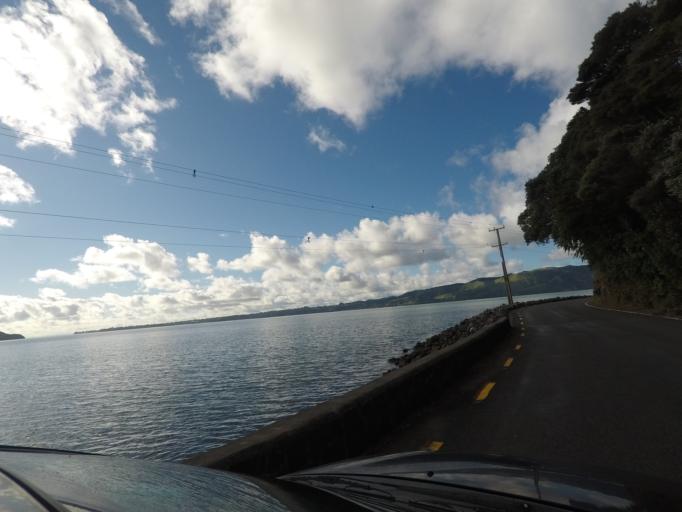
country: NZ
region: Auckland
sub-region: Auckland
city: Titirangi
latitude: -37.0101
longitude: 174.5625
